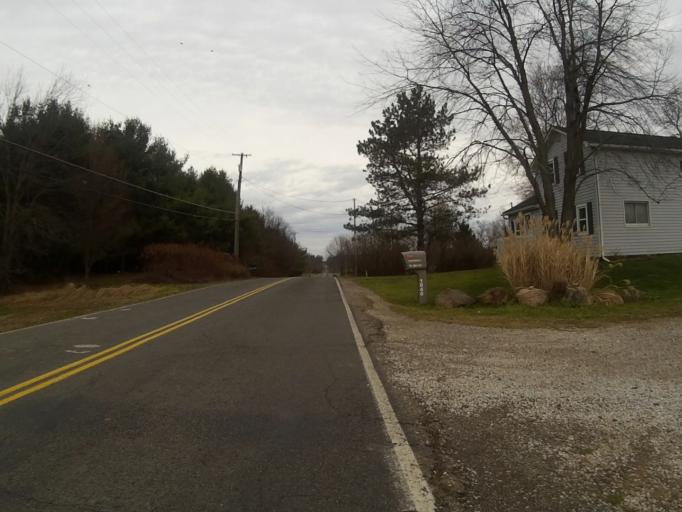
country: US
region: Ohio
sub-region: Stark County
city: Hartville
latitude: 41.0174
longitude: -81.3293
